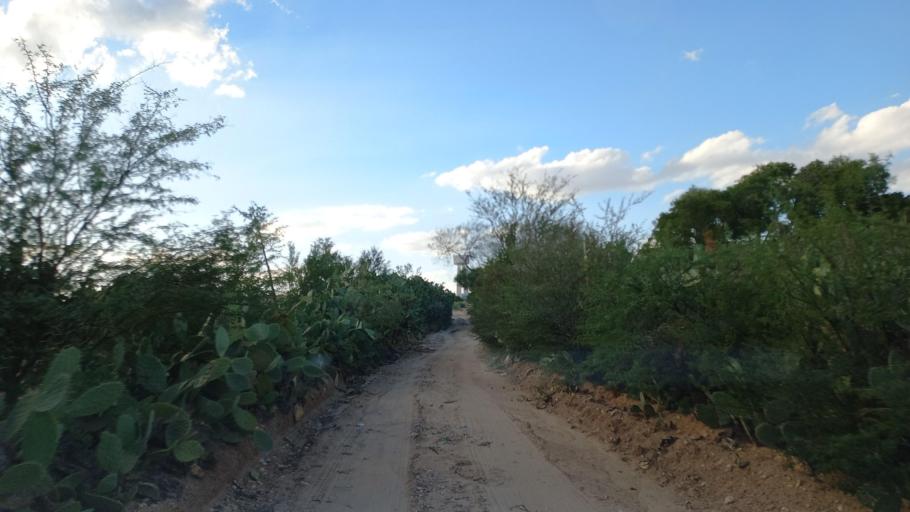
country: TN
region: Al Qasrayn
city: Sbiba
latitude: 35.3883
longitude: 9.0475
